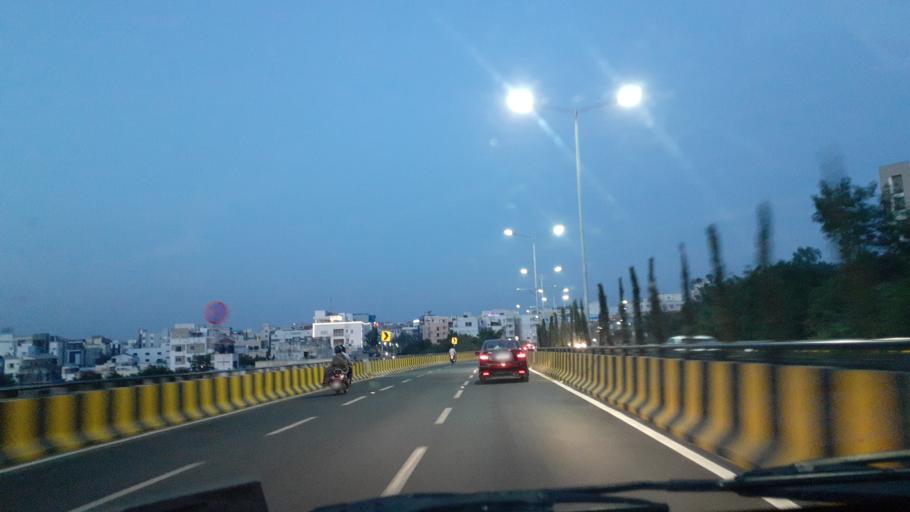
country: IN
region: Telangana
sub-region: Rangareddi
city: Kukatpalli
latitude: 17.4327
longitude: 78.3928
